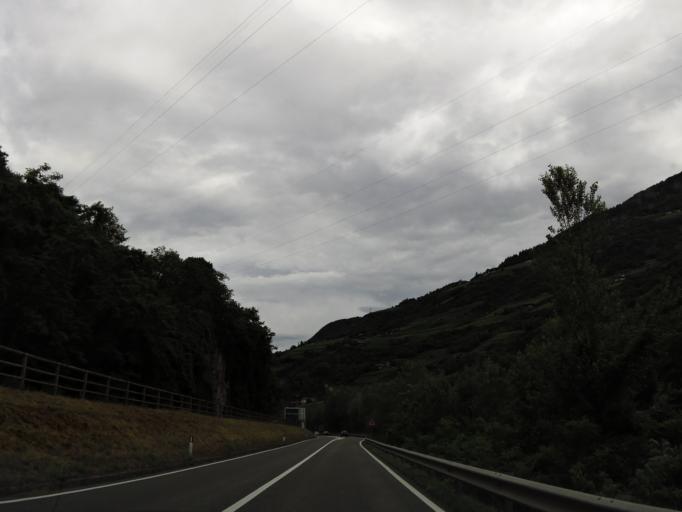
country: IT
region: Trentino-Alto Adige
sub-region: Bolzano
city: Cornedo All'Isarco
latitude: 46.4922
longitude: 11.4147
